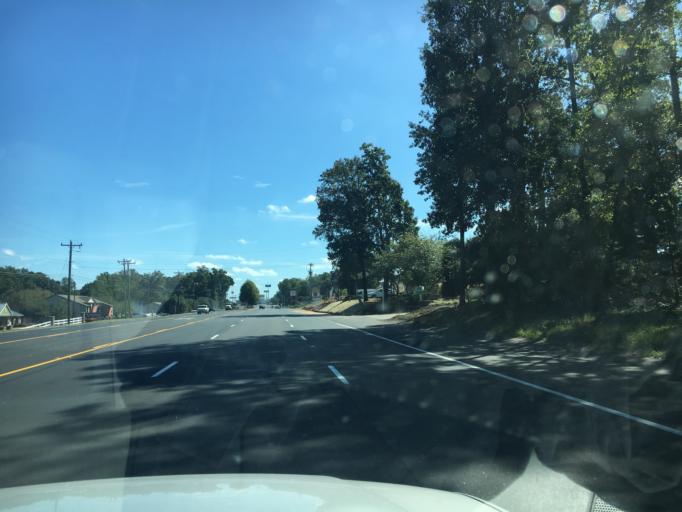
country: US
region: South Carolina
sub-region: Spartanburg County
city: Fairforest
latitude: 34.9361
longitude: -82.0134
